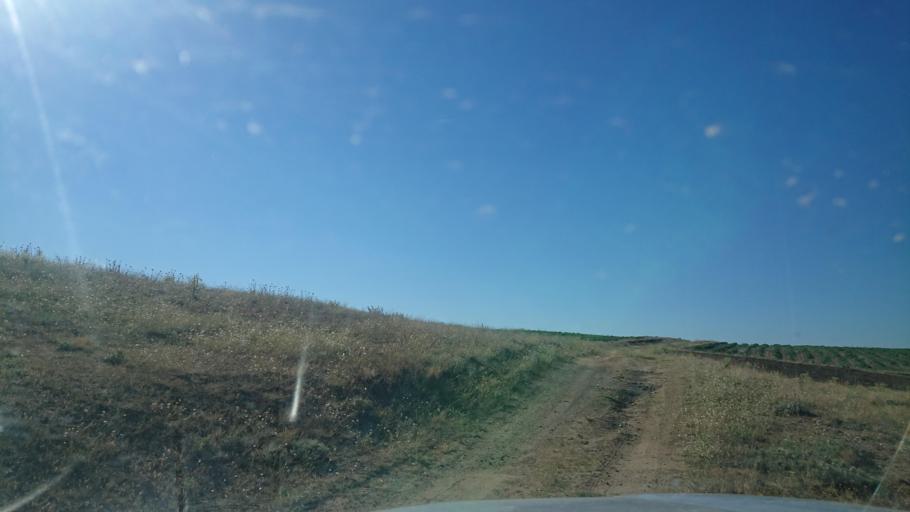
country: TR
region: Aksaray
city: Agacoren
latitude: 38.8377
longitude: 33.9370
